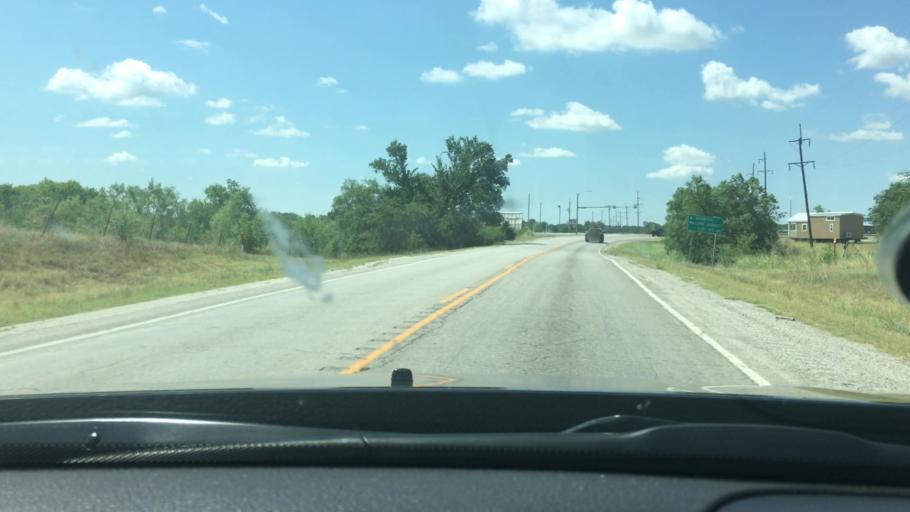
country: US
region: Oklahoma
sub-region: Carter County
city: Ardmore
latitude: 34.0732
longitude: -97.1429
